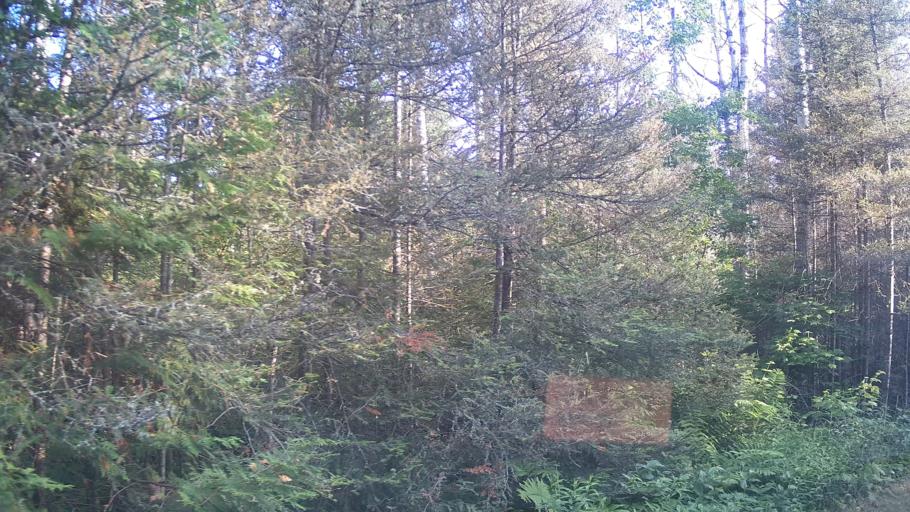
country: CA
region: Ontario
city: Rayside-Balfour
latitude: 46.5740
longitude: -81.3130
